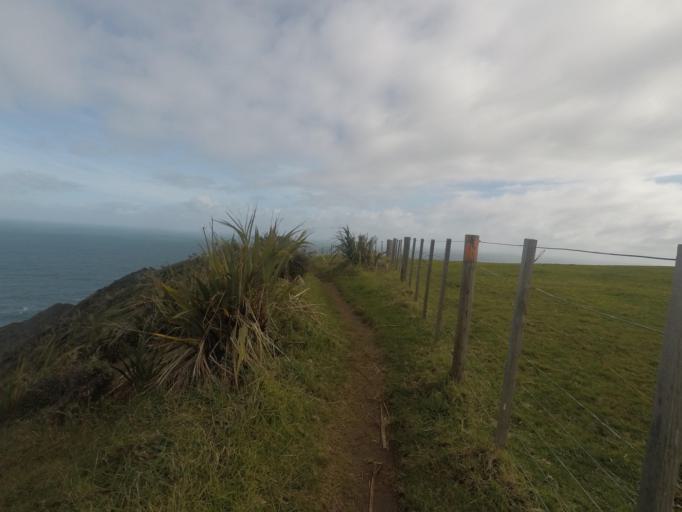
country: NZ
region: Auckland
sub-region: Auckland
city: Muriwai Beach
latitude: -36.8780
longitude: 174.4354
